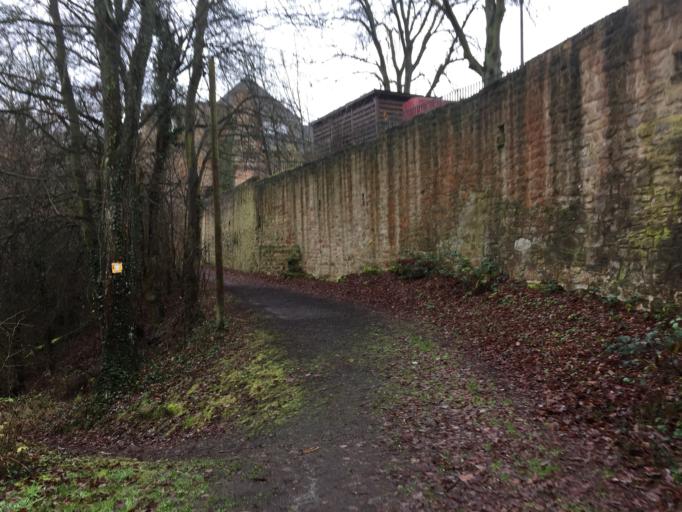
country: DE
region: Rheinland-Pfalz
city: Altleiningen
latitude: 49.5119
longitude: 8.0814
